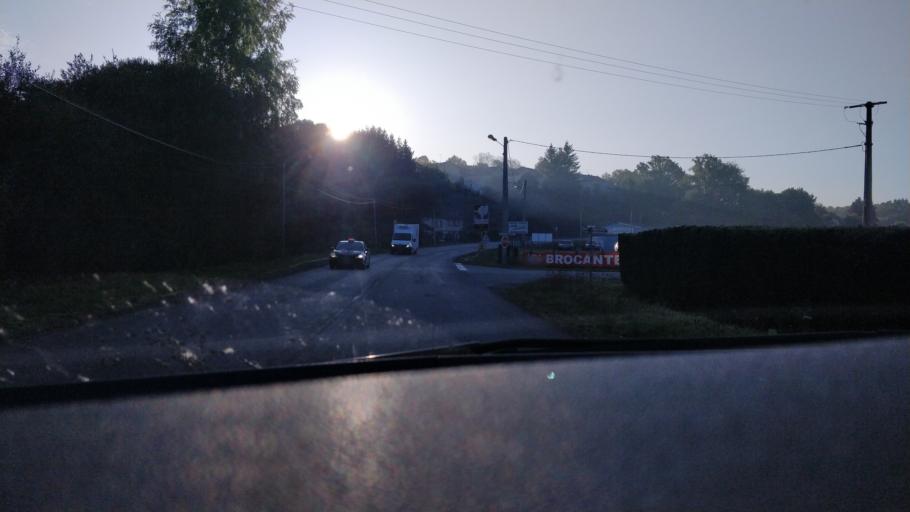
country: FR
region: Limousin
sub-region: Departement de la Creuse
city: Bourganeuf
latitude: 45.9555
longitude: 1.7425
